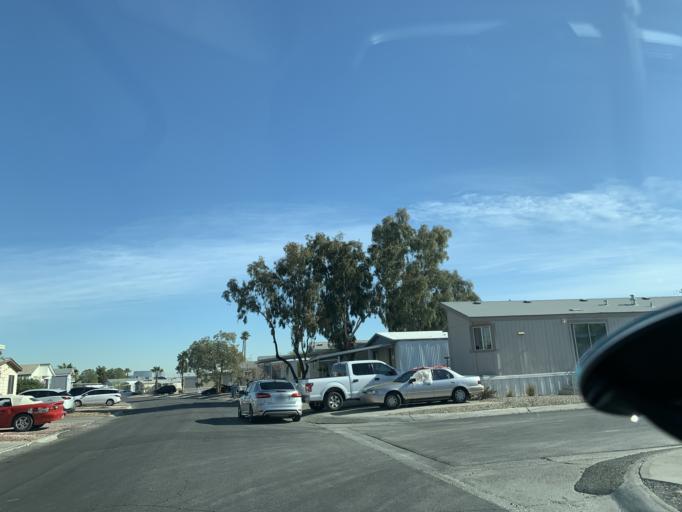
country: US
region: Nevada
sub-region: Clark County
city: Spring Valley
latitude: 36.1007
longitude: -115.2304
